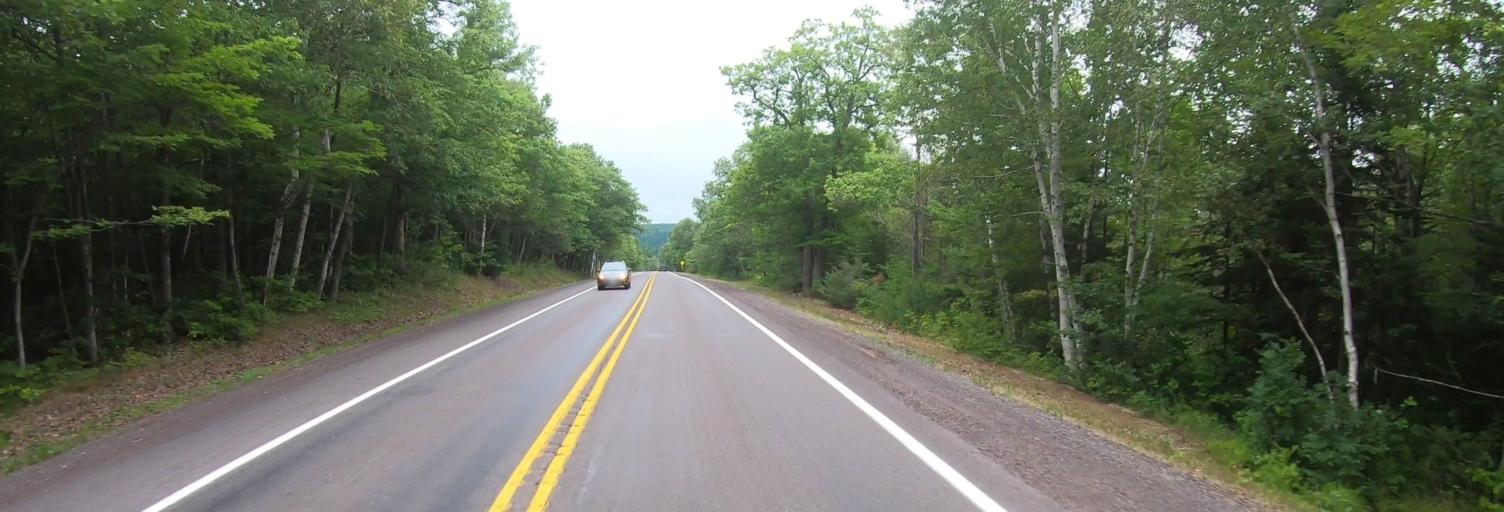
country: US
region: Michigan
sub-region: Keweenaw County
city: Eagle River
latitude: 47.3617
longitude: -88.3027
